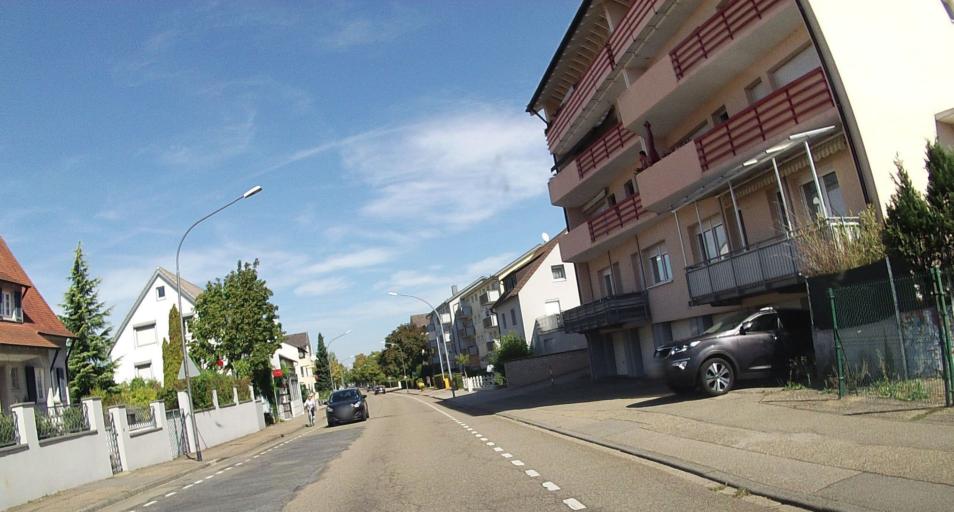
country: DE
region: Baden-Wuerttemberg
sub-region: Karlsruhe Region
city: Rastatt
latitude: 48.8471
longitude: 8.2068
